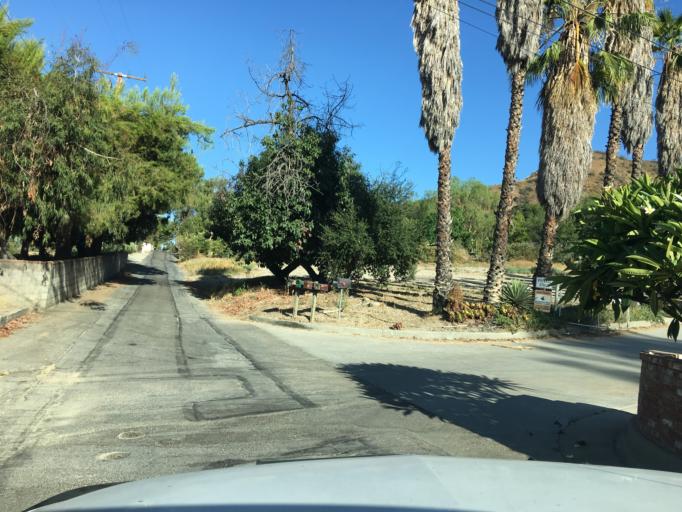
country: US
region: California
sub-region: Los Angeles County
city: Glendora
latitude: 34.1478
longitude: -117.8824
